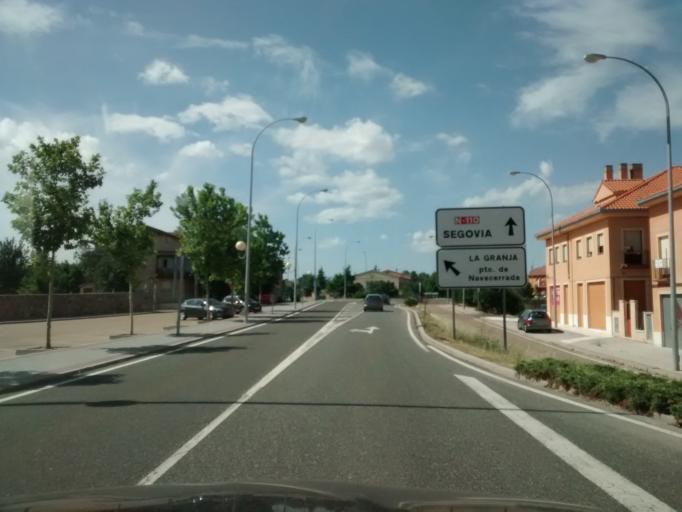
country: ES
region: Castille and Leon
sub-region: Provincia de Segovia
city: Torrecaballeros
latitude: 40.9953
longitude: -4.0219
